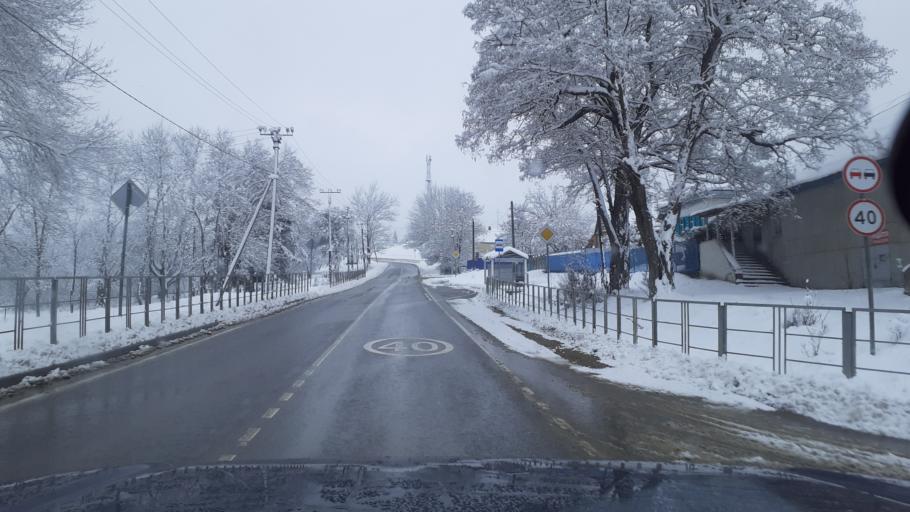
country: RU
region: Adygeya
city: Kamennomostskiy
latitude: 44.2316
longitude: 40.2018
